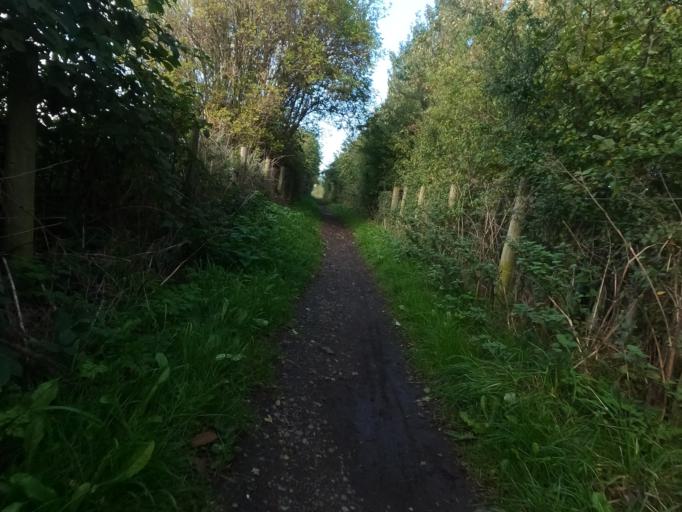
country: GB
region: England
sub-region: Northumberland
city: Seghill
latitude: 55.0705
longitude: -1.5403
